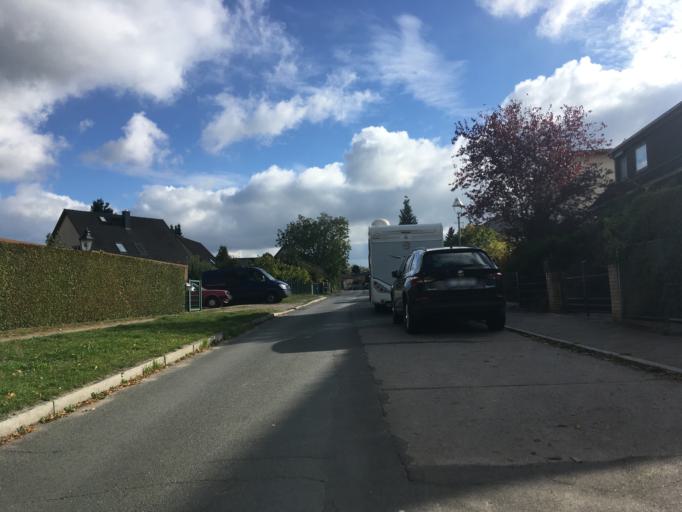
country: DE
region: Berlin
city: Rudow
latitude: 52.4070
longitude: 13.4850
